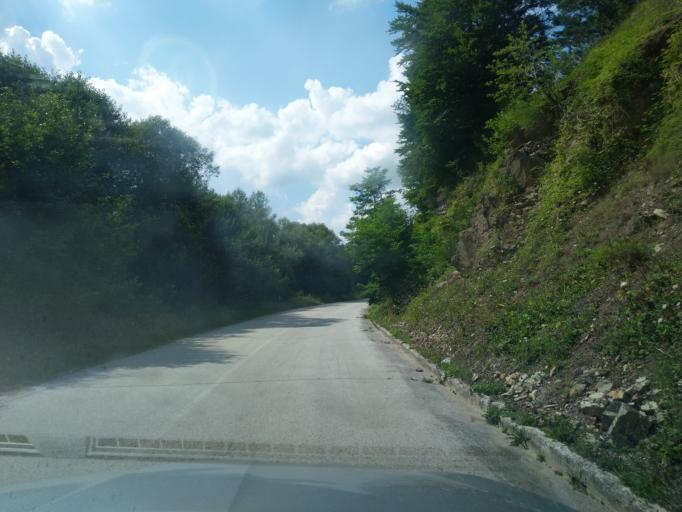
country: RS
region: Central Serbia
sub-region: Zlatiborski Okrug
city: Nova Varos
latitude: 43.5871
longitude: 19.8697
